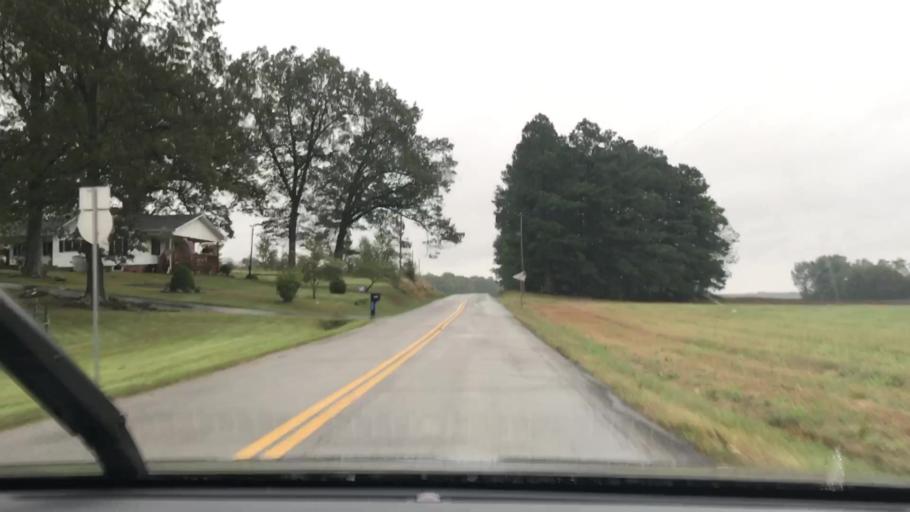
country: US
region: Kentucky
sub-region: Webster County
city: Sebree
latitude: 37.4897
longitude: -87.4708
